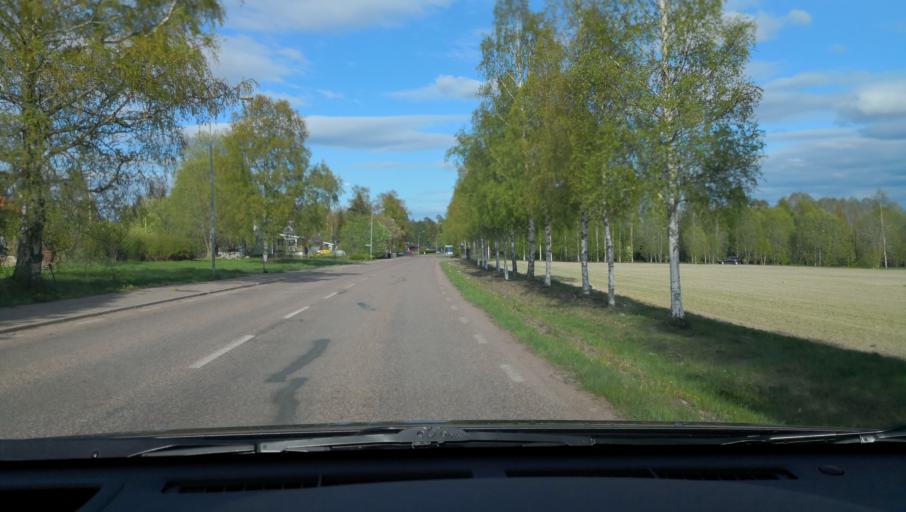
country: SE
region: Dalarna
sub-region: Saters Kommun
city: Saeter
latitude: 60.2991
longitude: 15.8304
